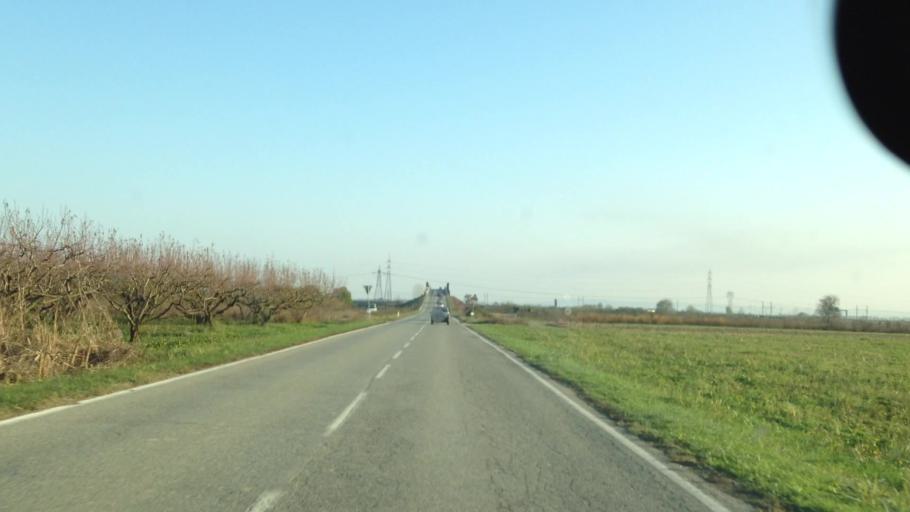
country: IT
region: Piedmont
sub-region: Provincia di Vercelli
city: Borgo d'Ale
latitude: 45.3339
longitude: 8.0780
